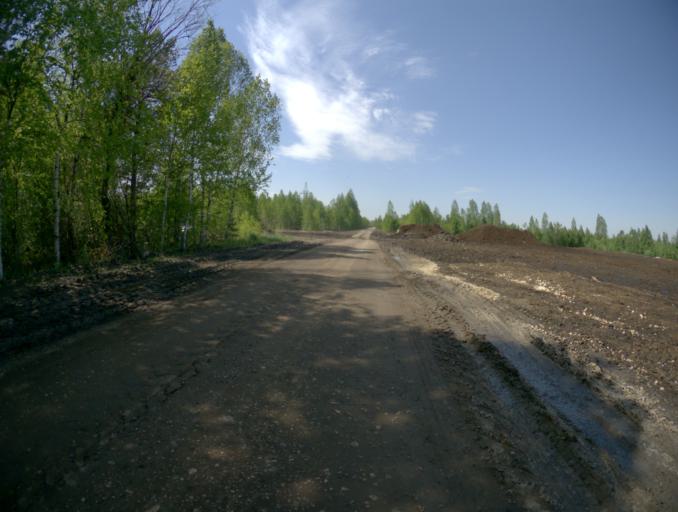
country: RU
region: Vladimir
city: Gusevskiy
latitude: 55.6914
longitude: 40.5385
